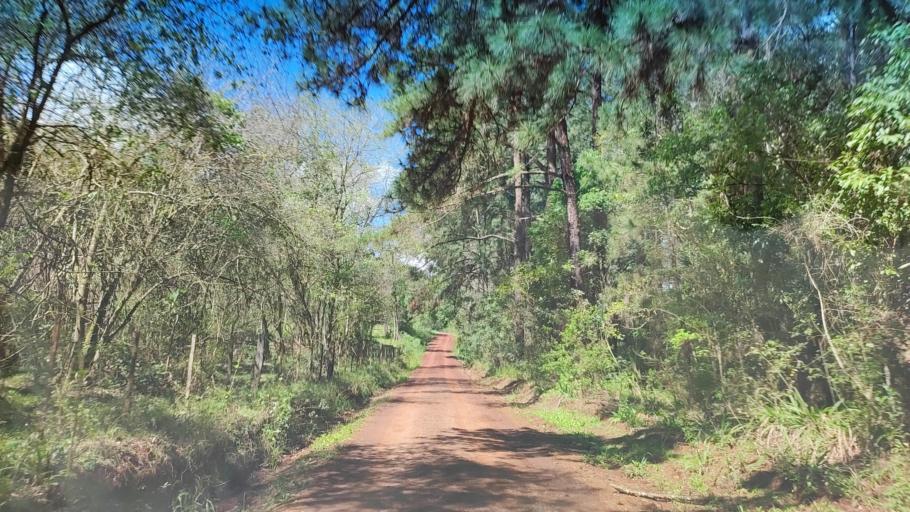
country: AR
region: Misiones
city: Ruiz de Montoya
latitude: -26.9529
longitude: -55.0309
